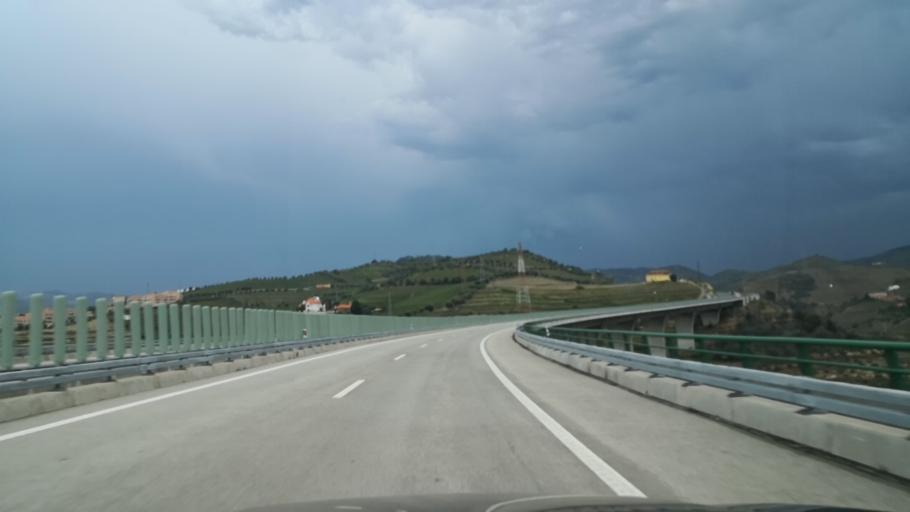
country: PT
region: Vila Real
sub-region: Peso da Regua
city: Peso da Regua
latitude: 41.1543
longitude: -7.7766
